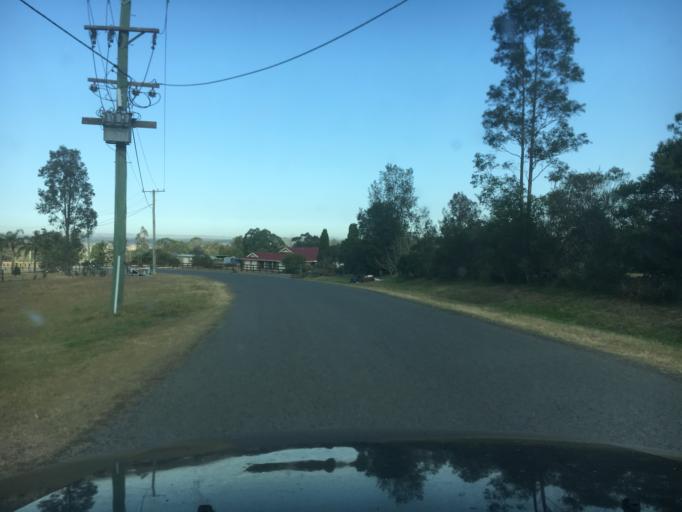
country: AU
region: New South Wales
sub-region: Cessnock
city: Branxton
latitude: -32.6432
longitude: 151.3725
